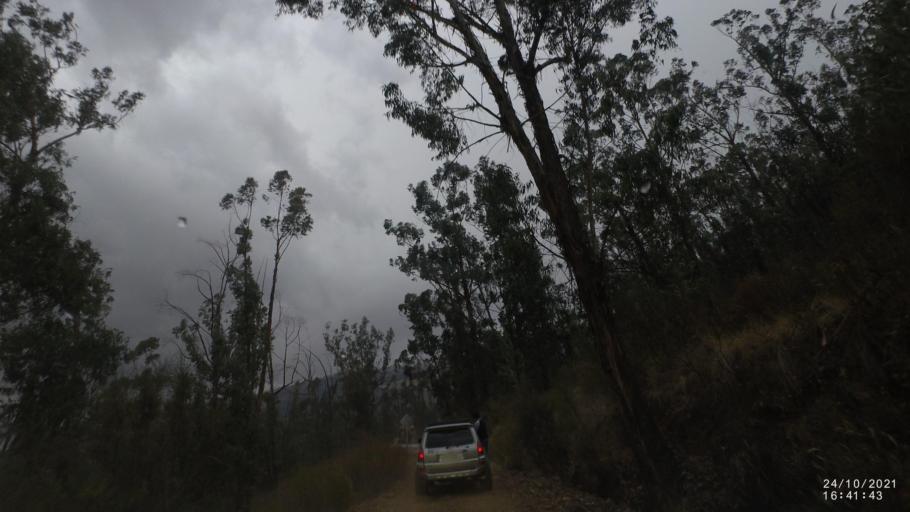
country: BO
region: Cochabamba
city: Cochabamba
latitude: -17.3421
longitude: -66.1475
